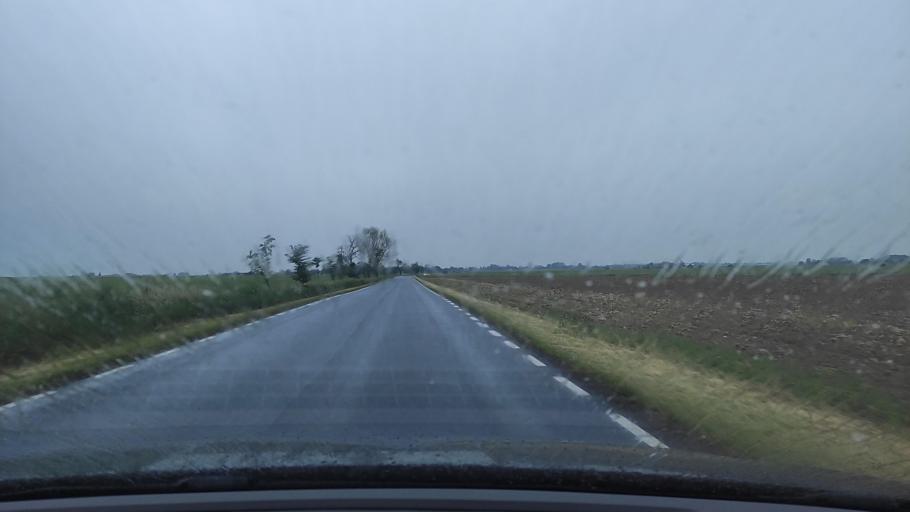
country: PL
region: Greater Poland Voivodeship
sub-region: Powiat poznanski
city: Kostrzyn
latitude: 52.4373
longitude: 17.1652
